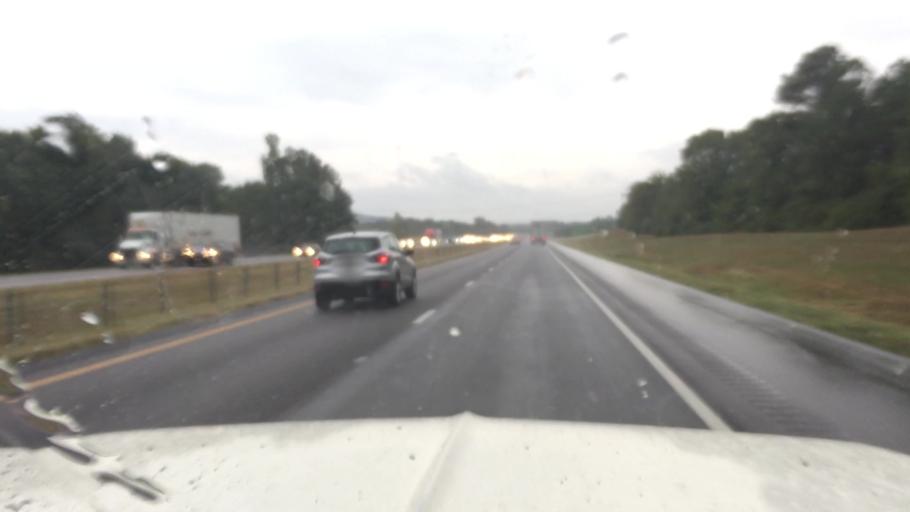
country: US
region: Alabama
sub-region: Morgan County
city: Hartselle
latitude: 34.4191
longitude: -86.8988
